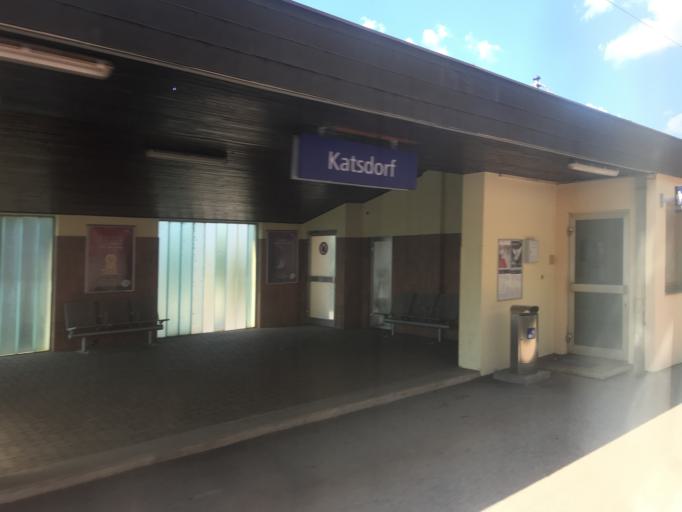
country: AT
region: Upper Austria
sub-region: Politischer Bezirk Urfahr-Umgebung
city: Engerwitzdorf
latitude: 48.3118
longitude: 14.4894
